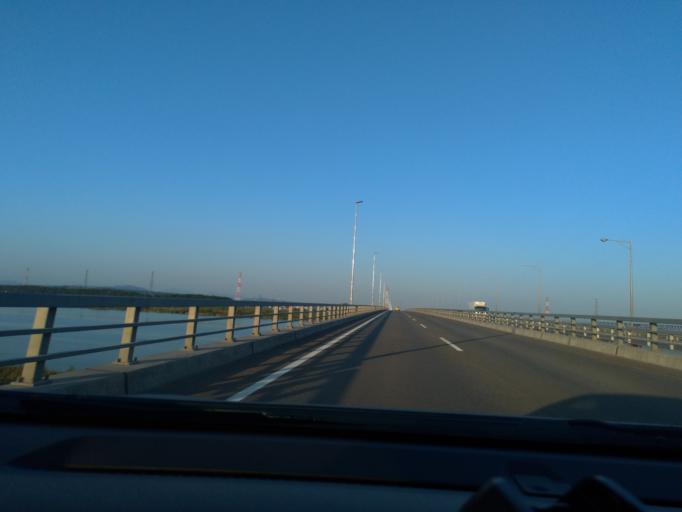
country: JP
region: Hokkaido
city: Ishikari
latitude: 43.1718
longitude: 141.4169
